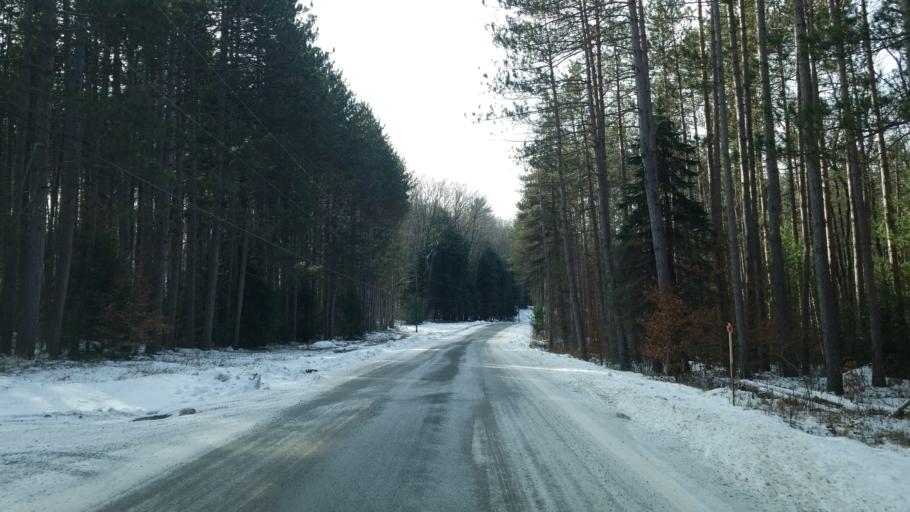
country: US
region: Pennsylvania
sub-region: Clearfield County
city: Clearfield
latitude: 41.1918
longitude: -78.5152
